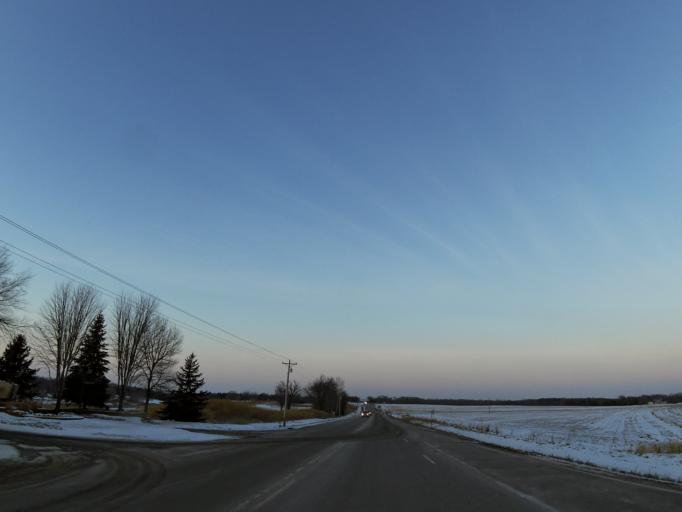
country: US
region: Minnesota
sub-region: Washington County
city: Lake Saint Croix Beach
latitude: 44.8994
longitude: -92.7313
